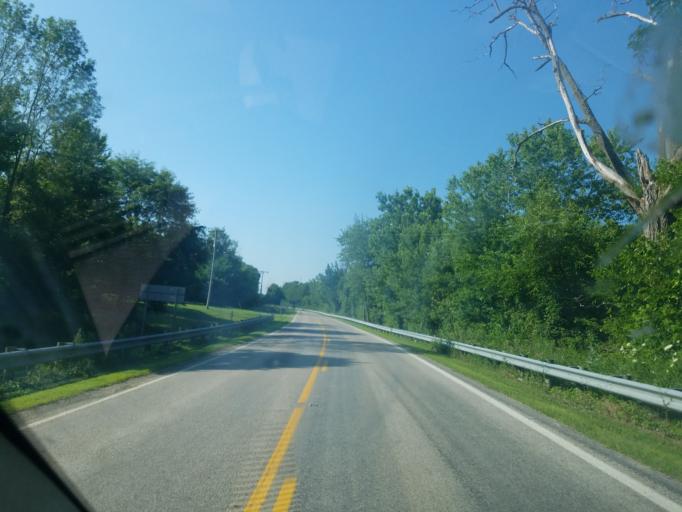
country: US
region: Ohio
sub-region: Marion County
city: Prospect
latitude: 40.4828
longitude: -83.1905
